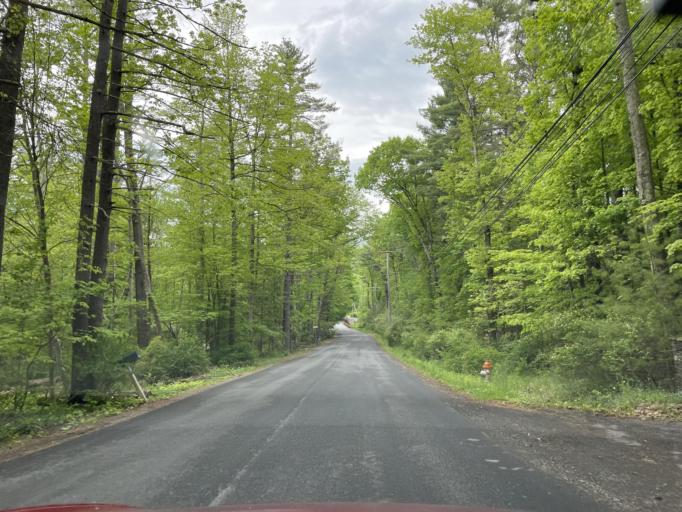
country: US
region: New York
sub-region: Ulster County
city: Woodstock
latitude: 42.0335
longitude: -74.1468
